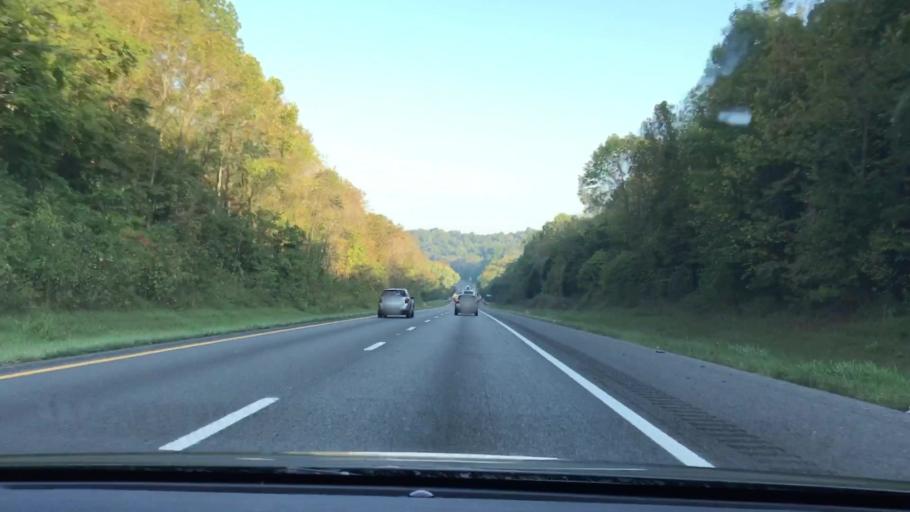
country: US
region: Tennessee
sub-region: Montgomery County
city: Clarksville
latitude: 36.5382
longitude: -87.2344
